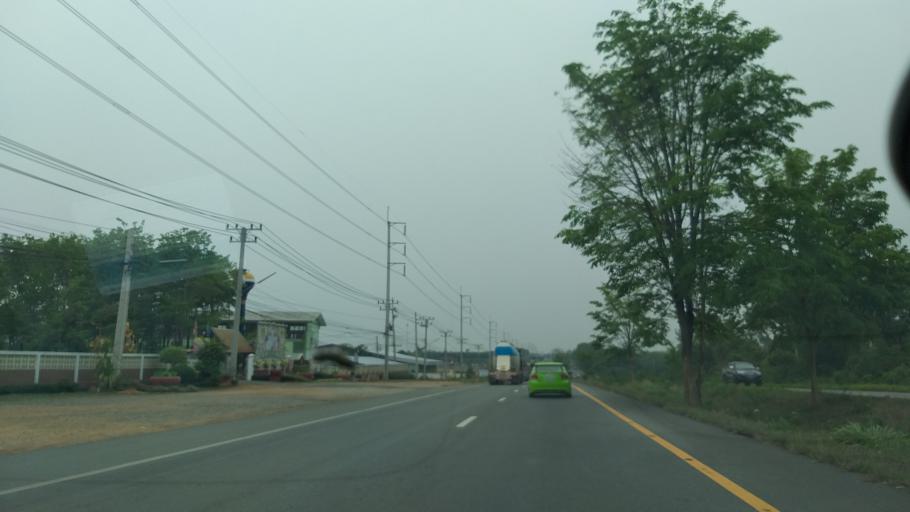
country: TH
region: Chon Buri
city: Ko Chan
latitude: 13.4527
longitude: 101.2837
